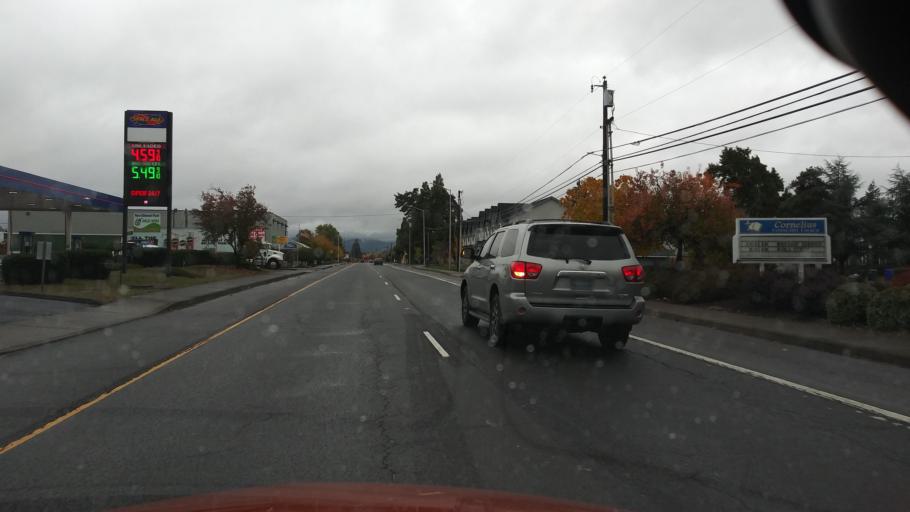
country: US
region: Oregon
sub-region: Washington County
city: Cornelius
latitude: 45.5209
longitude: -123.0609
